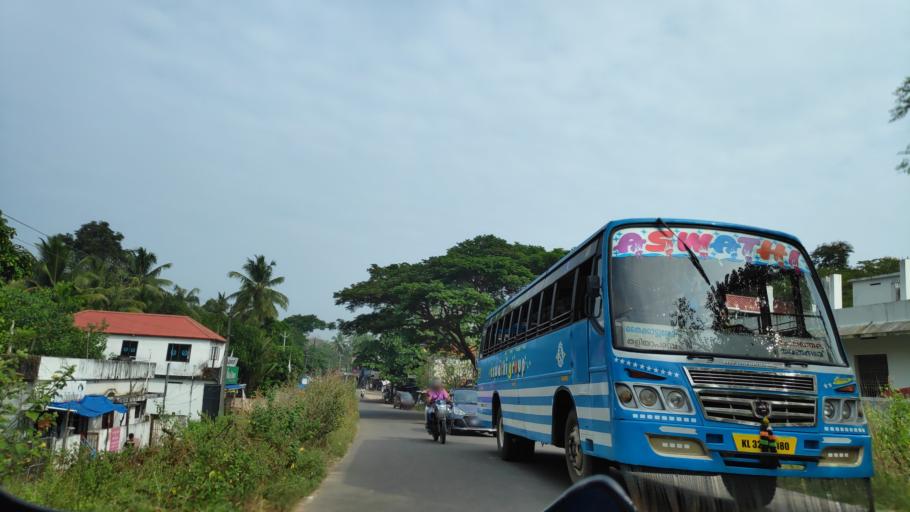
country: IN
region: Kerala
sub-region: Alappuzha
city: Kutiatodu
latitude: 9.7960
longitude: 76.3542
